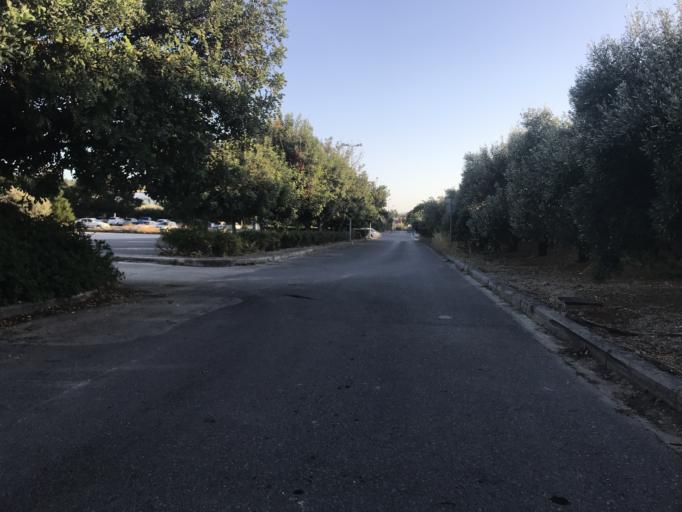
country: GR
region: Crete
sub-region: Nomos Irakleiou
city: Gazi
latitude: 35.3063
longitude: 25.0731
